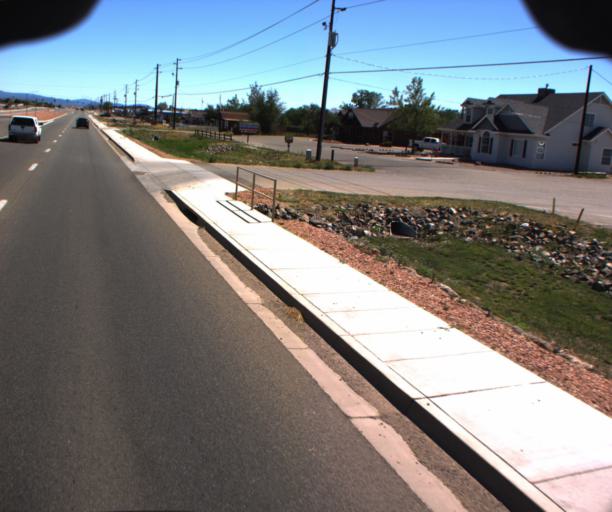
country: US
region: Arizona
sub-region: Yavapai County
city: Chino Valley
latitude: 34.7350
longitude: -112.4544
